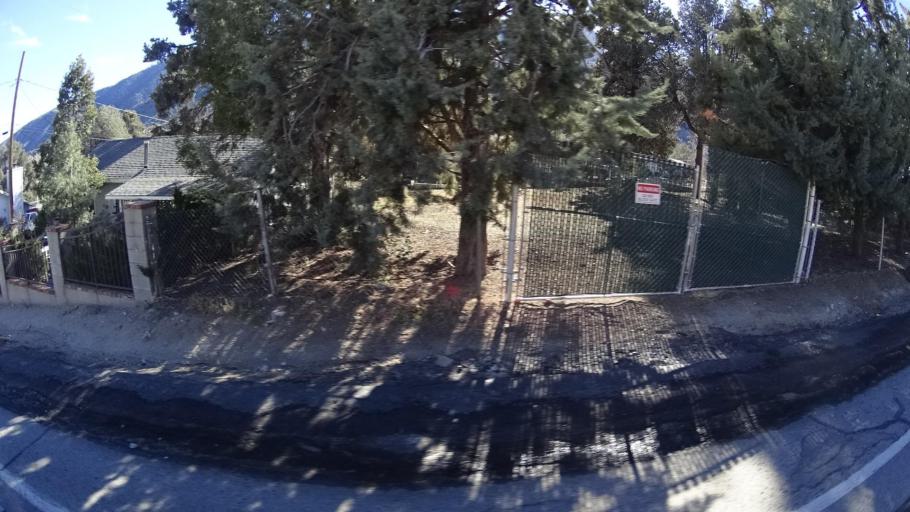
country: US
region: California
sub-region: Kern County
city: Frazier Park
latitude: 34.8228
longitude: -118.9524
